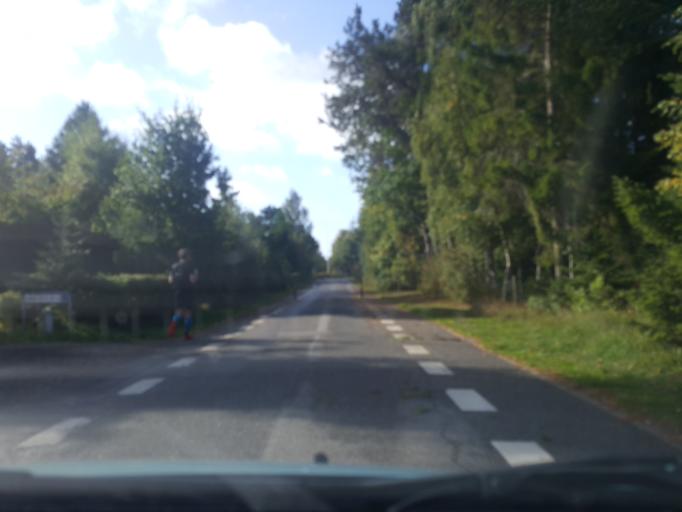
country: DK
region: Zealand
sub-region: Guldborgsund Kommune
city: Nykobing Falster
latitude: 54.6753
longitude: 11.9594
